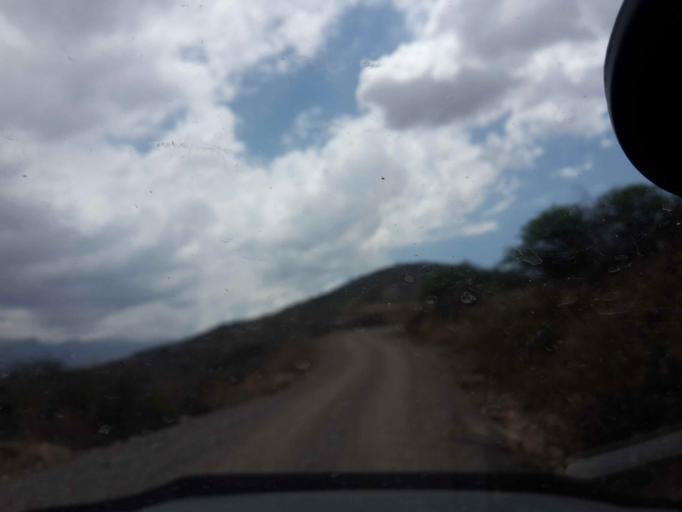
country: BO
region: Cochabamba
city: Sipe Sipe
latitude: -17.5336
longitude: -66.4923
